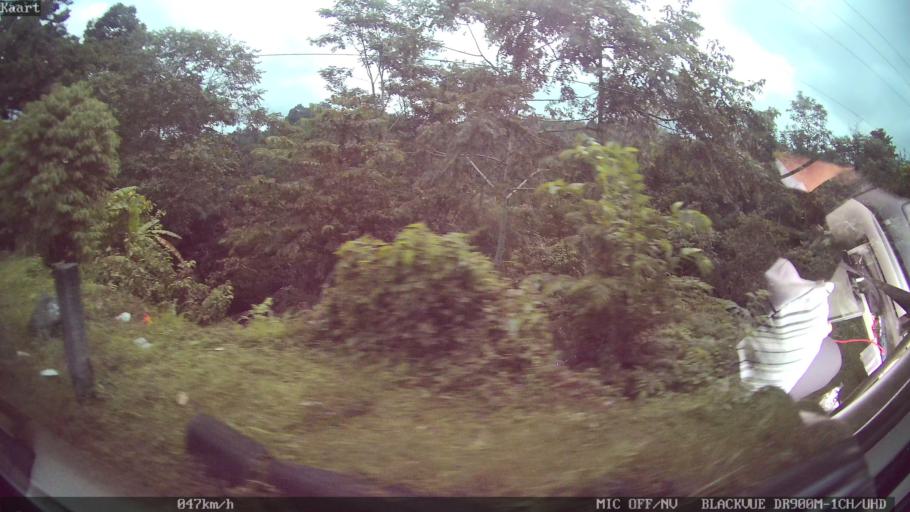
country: ID
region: Bali
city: Petang
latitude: -8.3782
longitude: 115.2236
